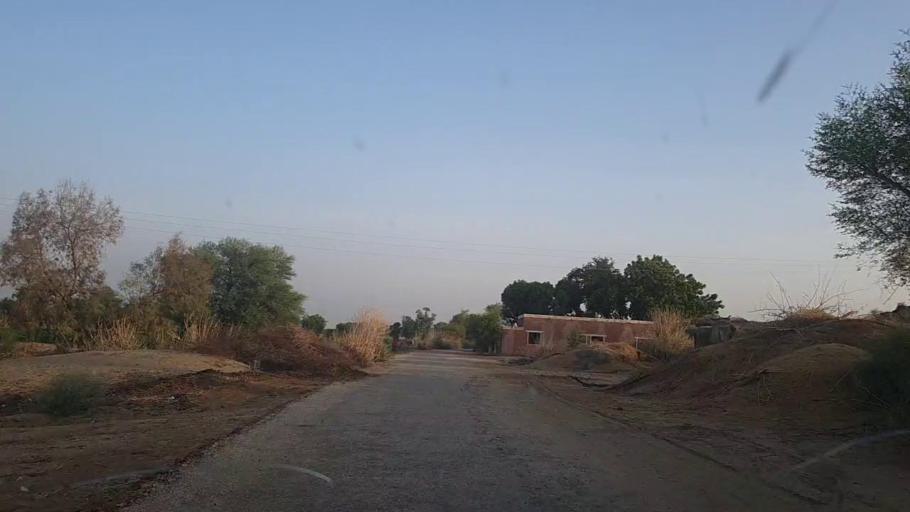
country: PK
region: Sindh
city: Khanpur
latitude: 27.6243
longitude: 69.4446
